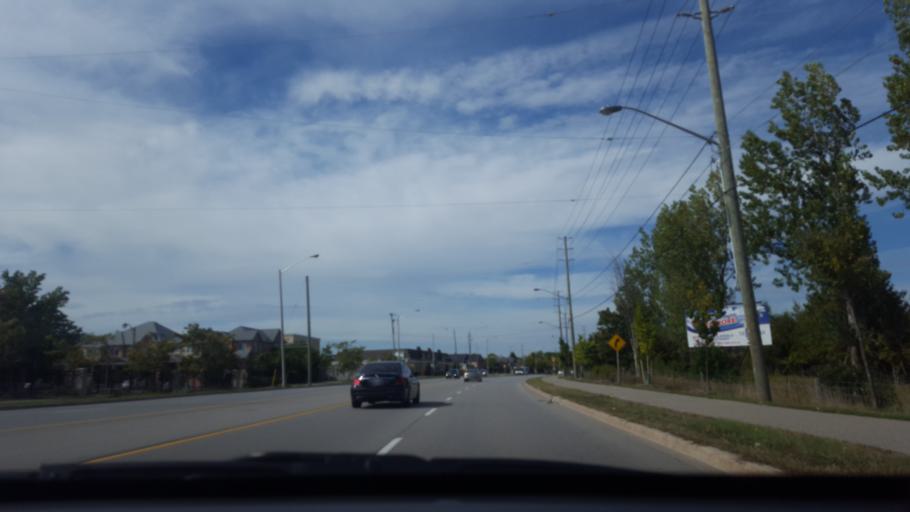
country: CA
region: Ontario
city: Vaughan
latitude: 43.8202
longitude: -79.6050
